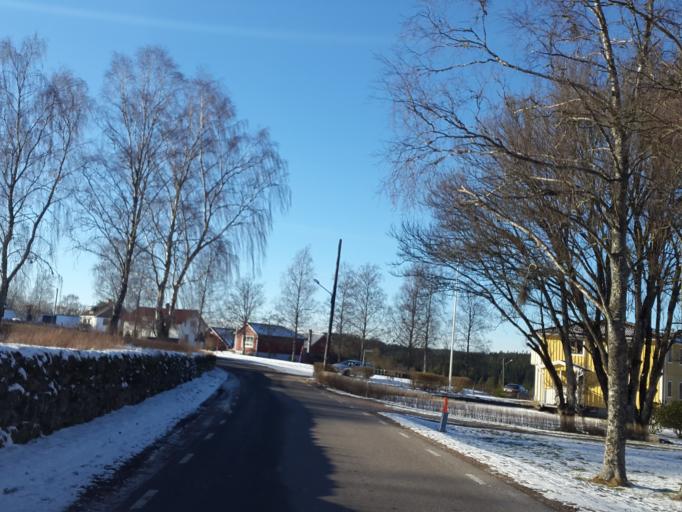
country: SE
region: Vaestra Goetaland
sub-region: Boras Kommun
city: Sandared
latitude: 57.8090
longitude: 12.7478
